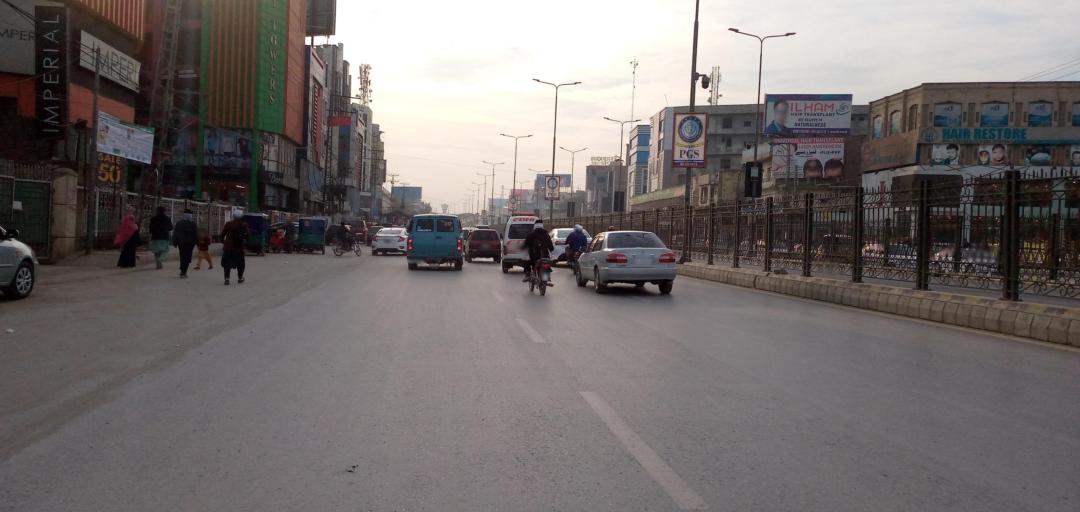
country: PK
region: Khyber Pakhtunkhwa
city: Peshawar
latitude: 34.0016
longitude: 71.4992
